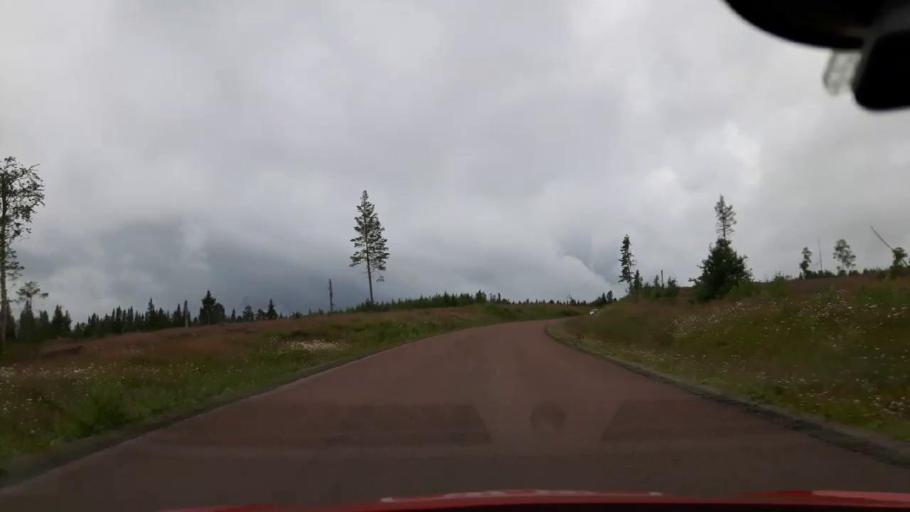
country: SE
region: Jaemtland
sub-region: Krokoms Kommun
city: Valla
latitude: 63.3731
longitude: 13.7570
